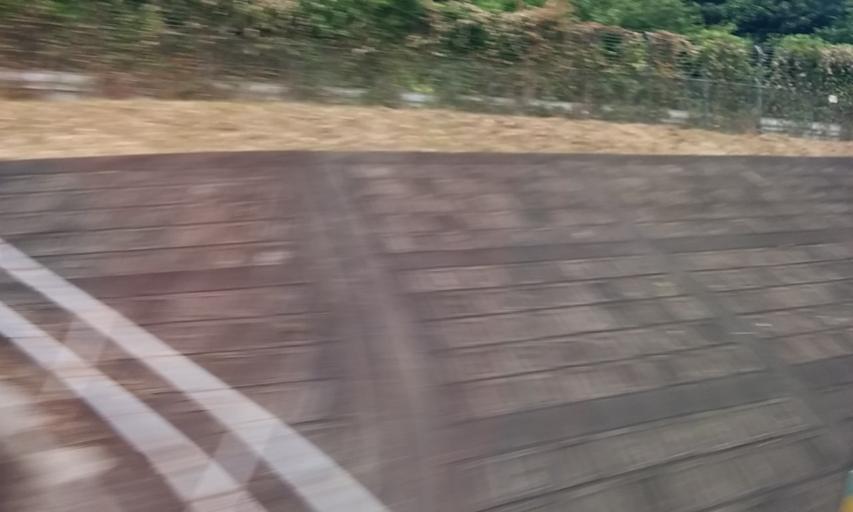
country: JP
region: Tochigi
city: Yaita
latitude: 36.7701
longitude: 139.9477
